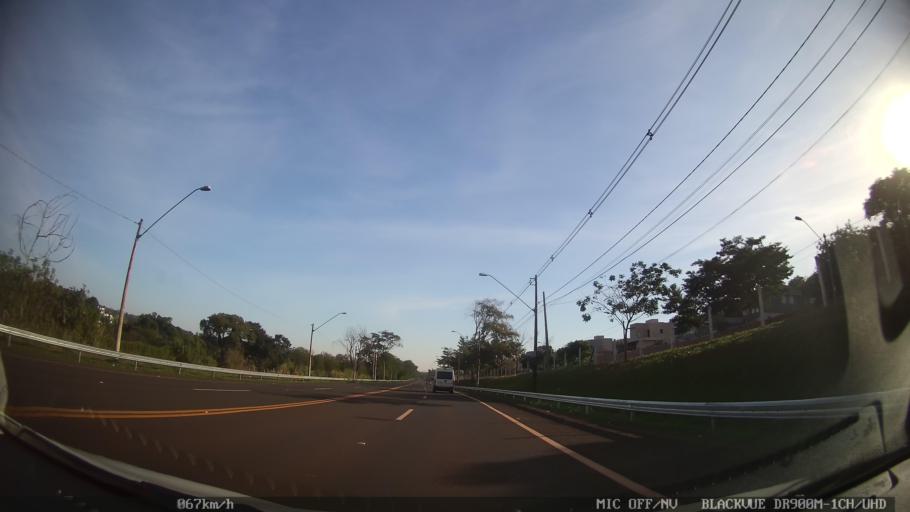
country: BR
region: Sao Paulo
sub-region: Cravinhos
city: Cravinhos
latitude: -21.2847
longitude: -47.8128
